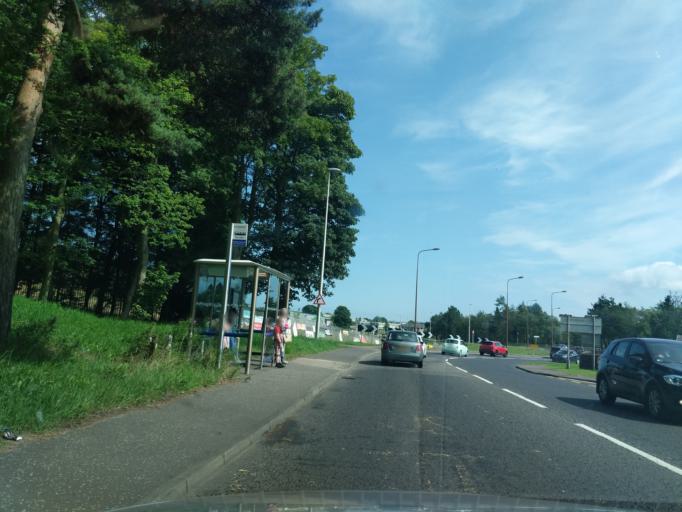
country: GB
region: Scotland
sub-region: Dundee City
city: Dundee
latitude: 56.4827
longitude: -3.0197
